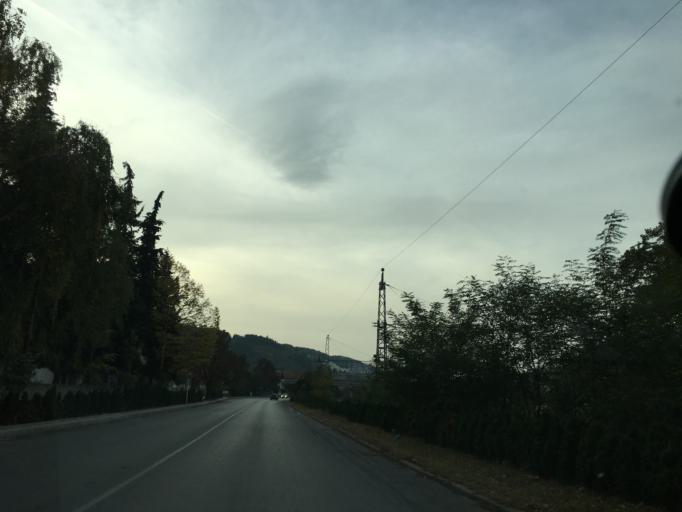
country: BG
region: Pazardzhik
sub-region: Obshtina Belovo
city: Belovo
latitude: 42.2163
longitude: 24.0121
